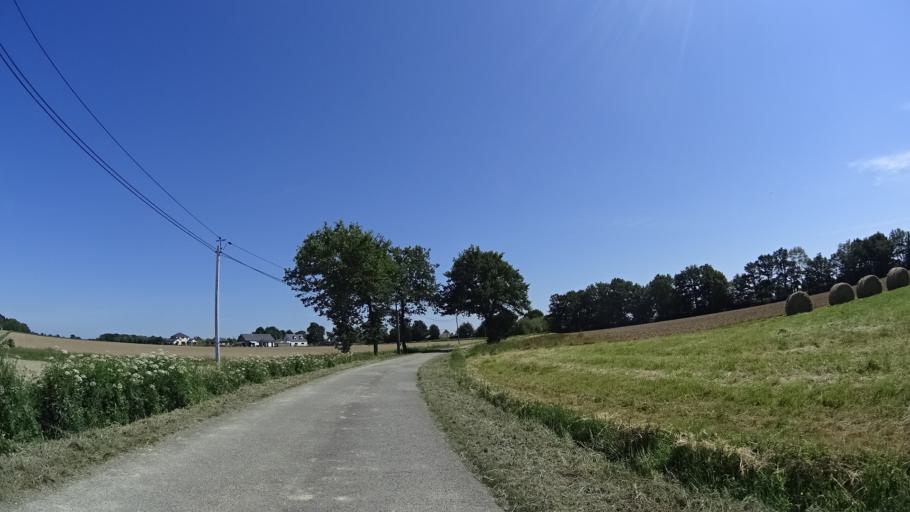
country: FR
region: Brittany
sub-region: Departement d'Ille-et-Vilaine
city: Messac
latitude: 47.7994
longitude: -1.8093
